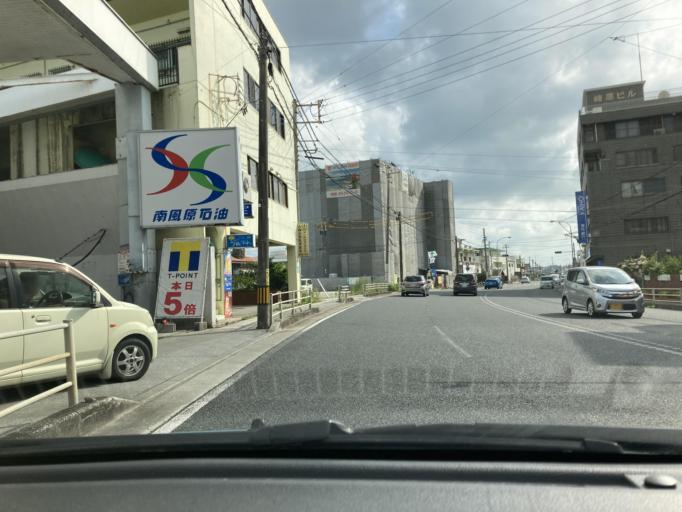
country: JP
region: Okinawa
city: Ginowan
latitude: 26.2205
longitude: 127.7654
